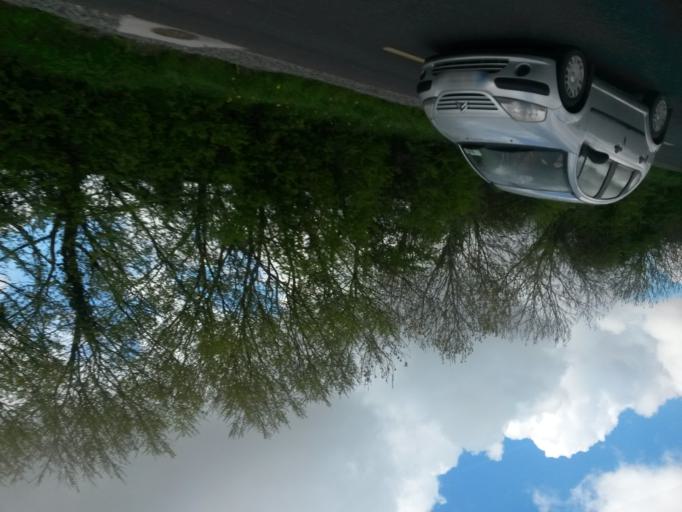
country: IE
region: Leinster
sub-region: Loch Garman
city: Castlebridge
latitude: 52.4129
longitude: -6.5238
